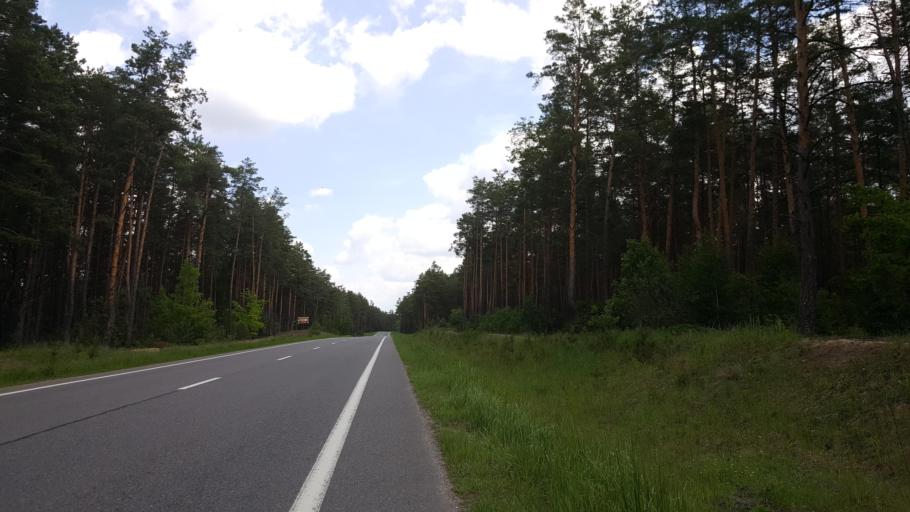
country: BY
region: Brest
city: Zhabinka
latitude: 52.4329
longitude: 24.1267
